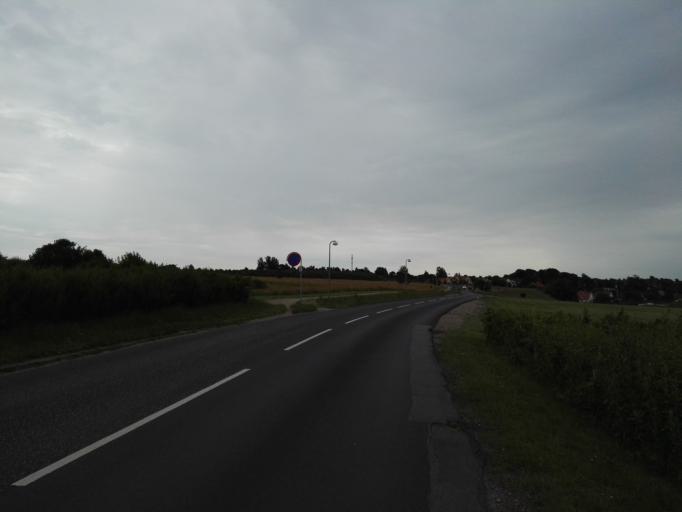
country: DK
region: Zealand
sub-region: Roskilde Kommune
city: Jyllinge
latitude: 55.7590
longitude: 12.0988
